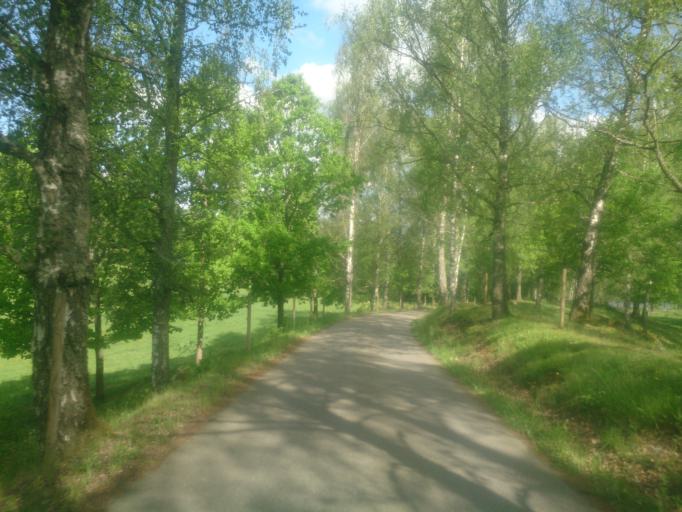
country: SE
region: OEstergoetland
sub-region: Atvidabergs Kommun
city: Atvidaberg
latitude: 58.3035
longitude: 16.0766
